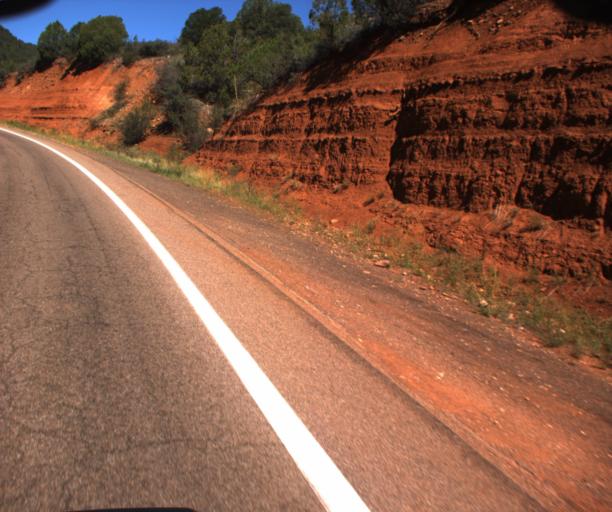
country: US
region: Arizona
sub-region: Navajo County
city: Cibecue
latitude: 33.9325
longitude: -110.3461
